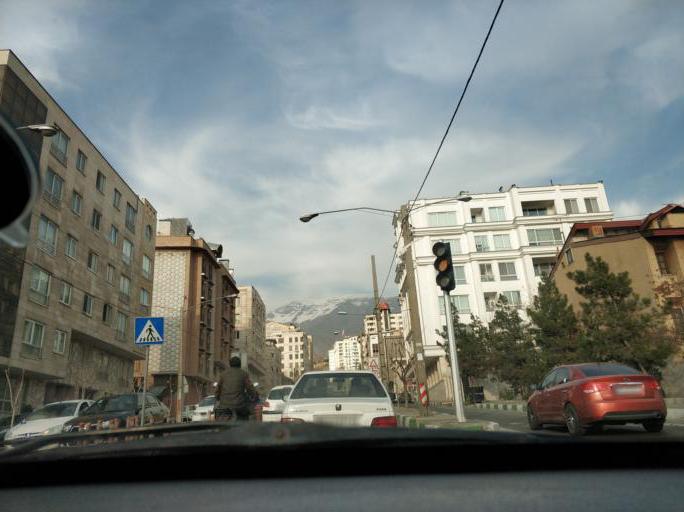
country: IR
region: Tehran
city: Tajrish
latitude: 35.8074
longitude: 51.4833
